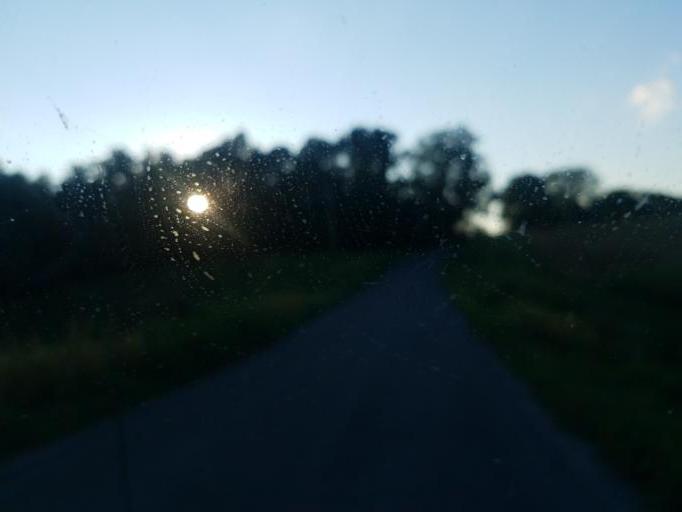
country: US
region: Illinois
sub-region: Jackson County
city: Murphysboro
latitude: 37.6755
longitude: -89.3084
